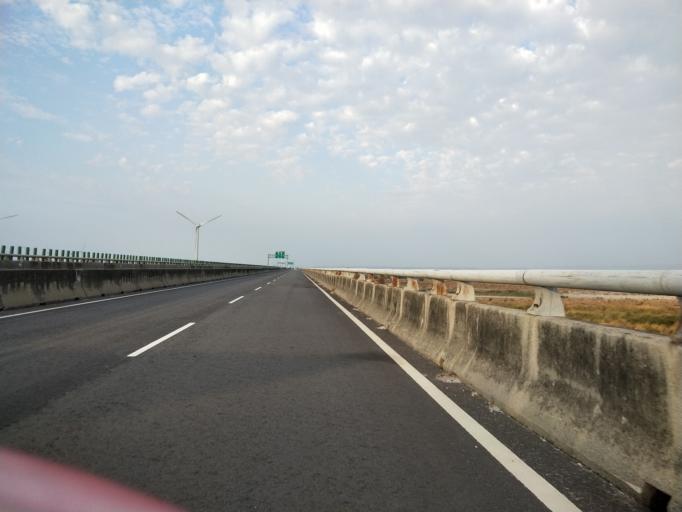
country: TW
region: Taiwan
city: Fengyuan
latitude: 24.3974
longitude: 120.6075
